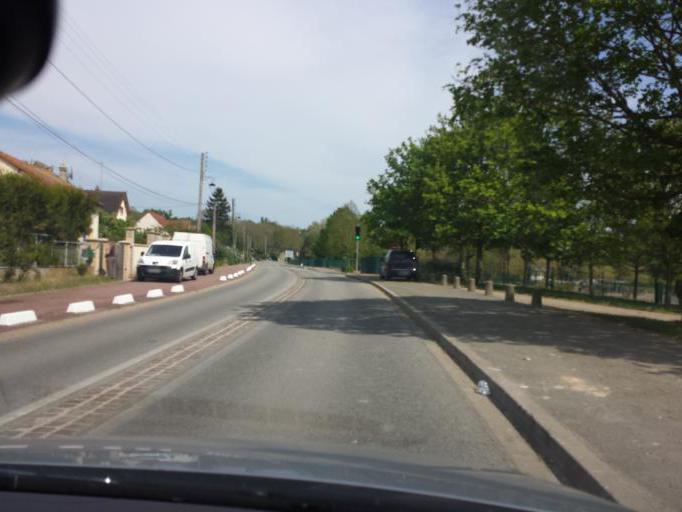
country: FR
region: Ile-de-France
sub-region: Departement des Yvelines
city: Villiers-Saint-Frederic
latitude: 48.8145
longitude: 1.8720
